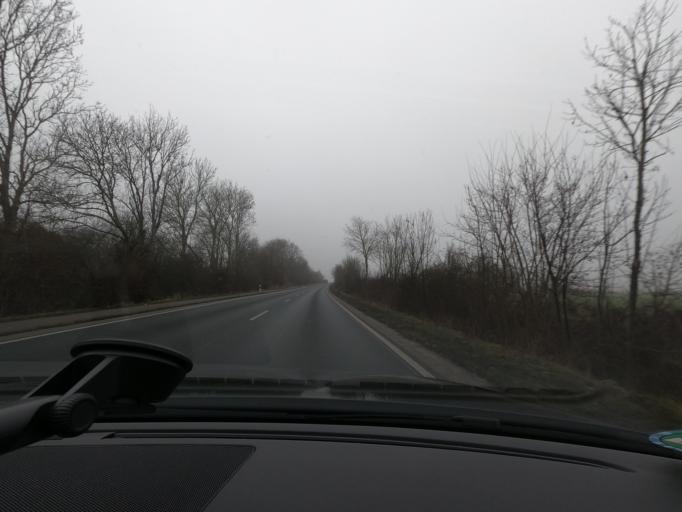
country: DE
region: North Rhine-Westphalia
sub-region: Regierungsbezirk Koln
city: Kreuzau
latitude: 50.7712
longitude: 6.5187
